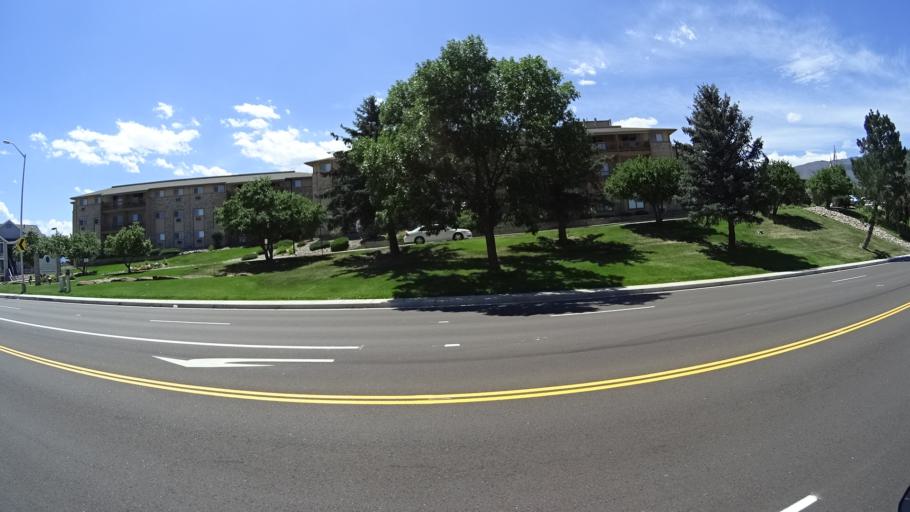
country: US
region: Colorado
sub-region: El Paso County
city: Air Force Academy
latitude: 38.9194
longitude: -104.8386
